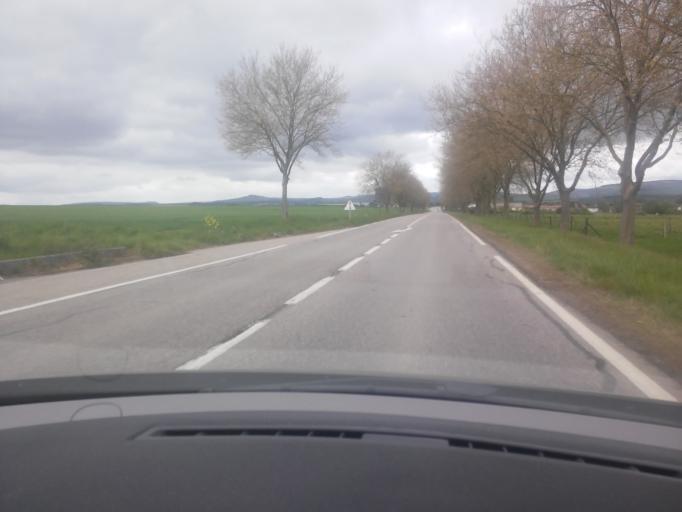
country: FR
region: Lorraine
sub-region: Departement de la Moselle
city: Verny
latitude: 48.9606
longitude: 6.1991
